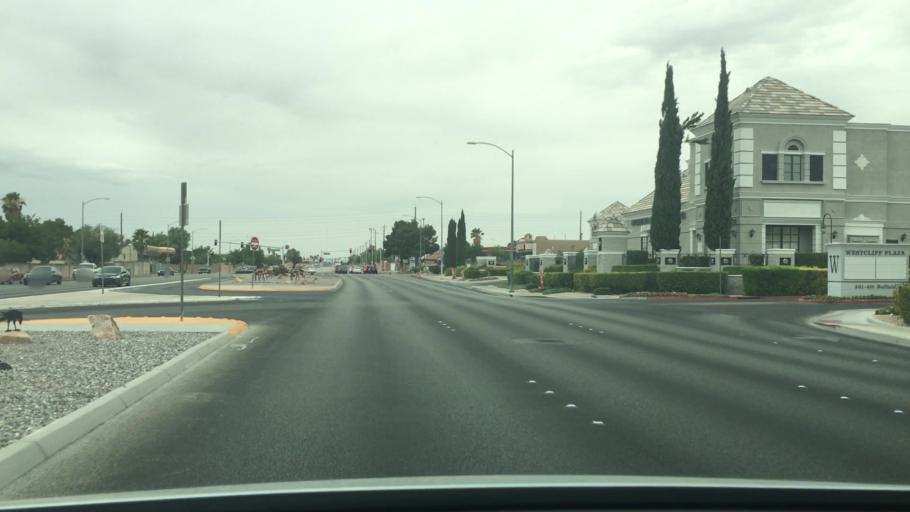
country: US
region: Nevada
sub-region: Clark County
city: Spring Valley
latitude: 36.1762
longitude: -115.2599
